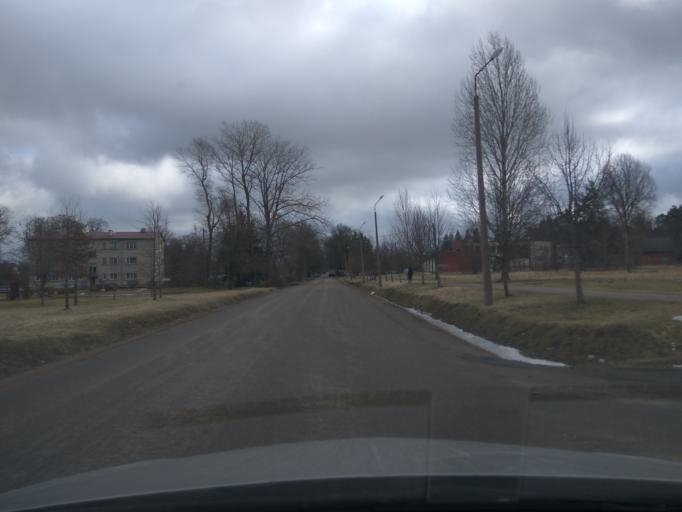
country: LV
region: Kuldigas Rajons
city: Kuldiga
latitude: 57.2774
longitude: 22.0184
